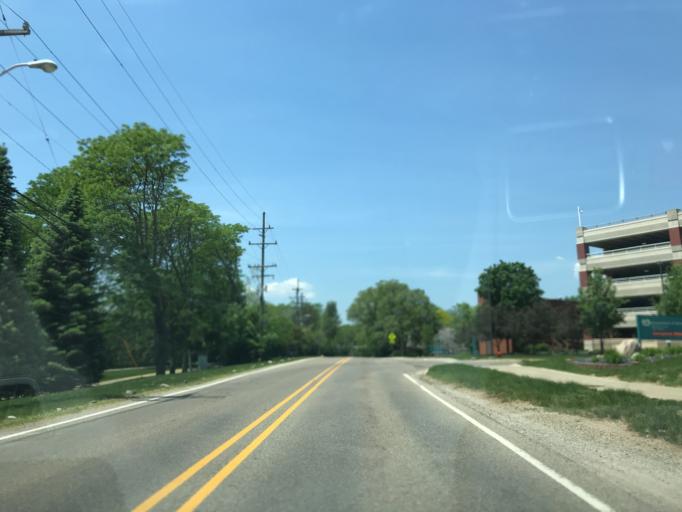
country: US
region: Michigan
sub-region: Washtenaw County
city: Ann Arbor
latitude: 42.2859
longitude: -83.7166
